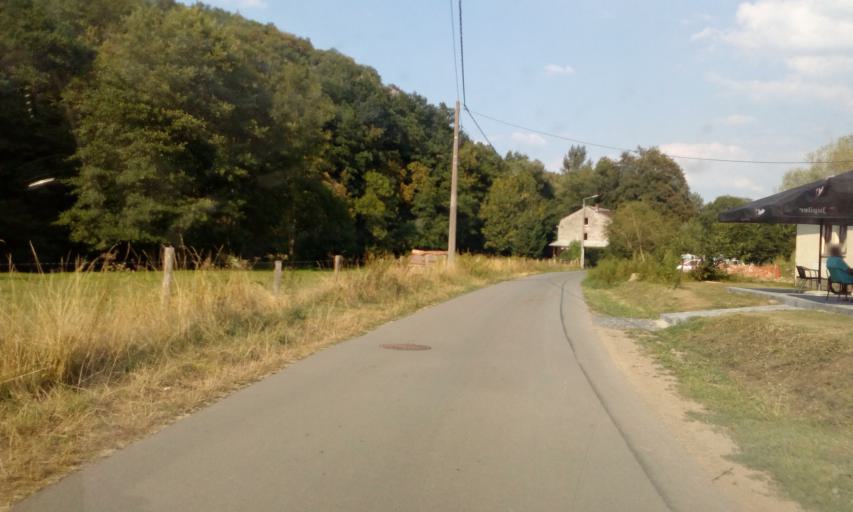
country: BE
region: Wallonia
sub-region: Province du Luxembourg
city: Tellin
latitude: 50.1093
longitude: 5.1976
